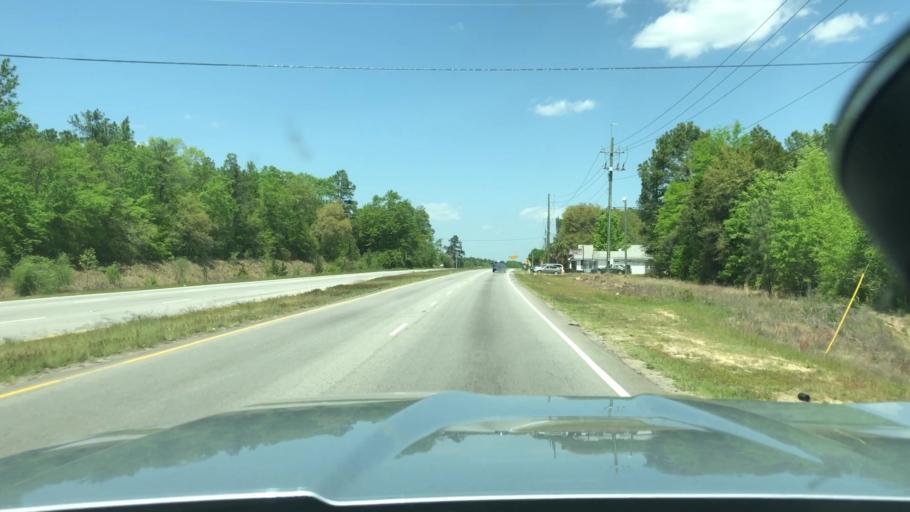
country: US
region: South Carolina
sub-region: Lexington County
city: Pineridge
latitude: 33.8976
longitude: -81.0630
